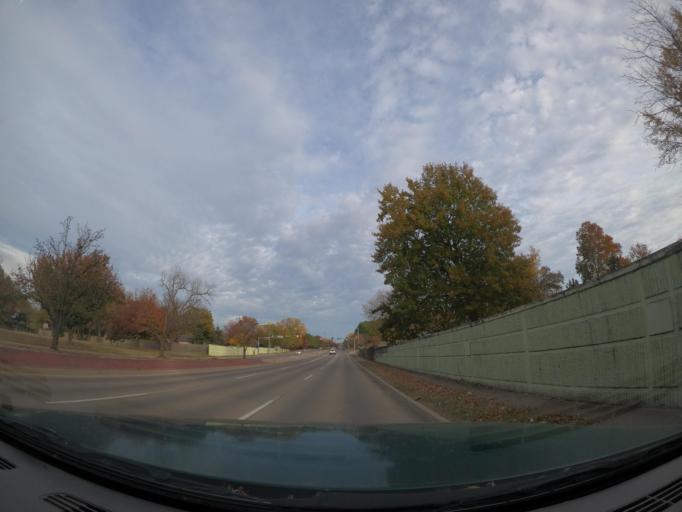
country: US
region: Oklahoma
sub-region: Tulsa County
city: Jenks
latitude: 36.0608
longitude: -95.9328
